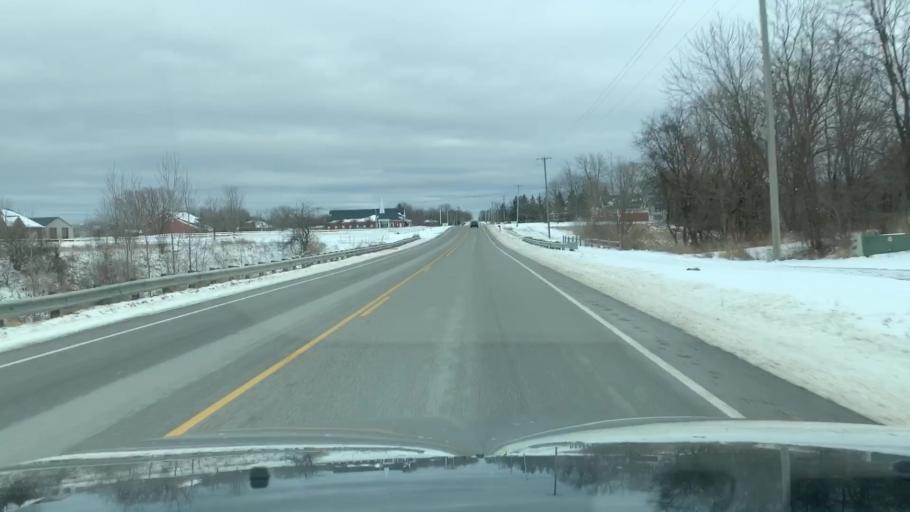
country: US
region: Michigan
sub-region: Ottawa County
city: Zeeland
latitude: 42.8121
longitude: -85.9559
